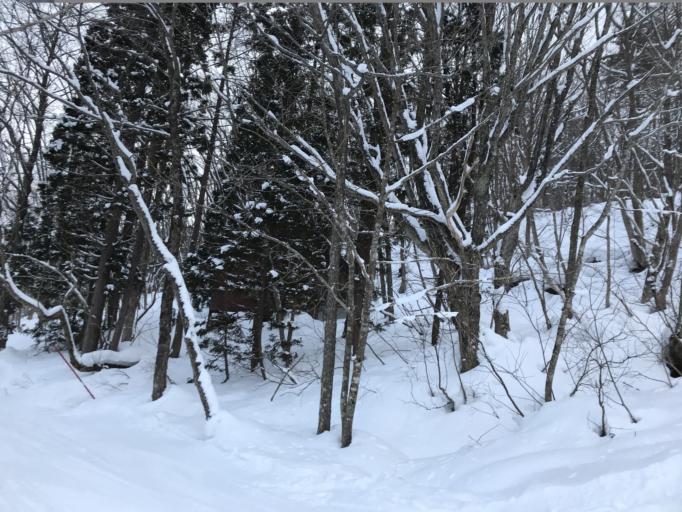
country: JP
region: Nagano
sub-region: Kitaazumi Gun
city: Hakuba
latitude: 36.7055
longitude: 137.8318
